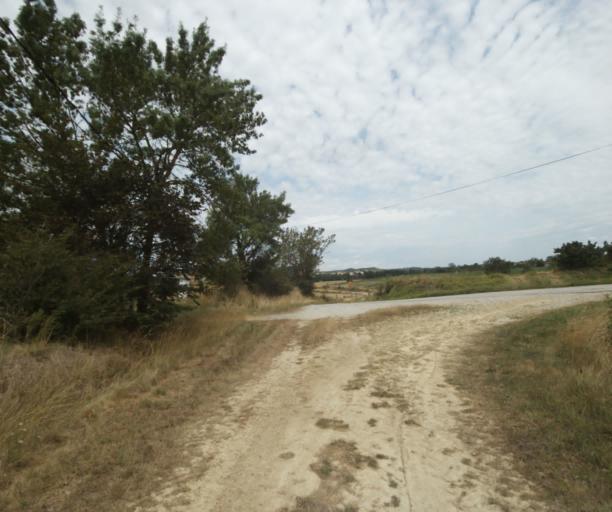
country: FR
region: Midi-Pyrenees
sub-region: Departement de la Haute-Garonne
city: Saint-Felix-Lauragais
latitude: 43.4160
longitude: 1.9066
